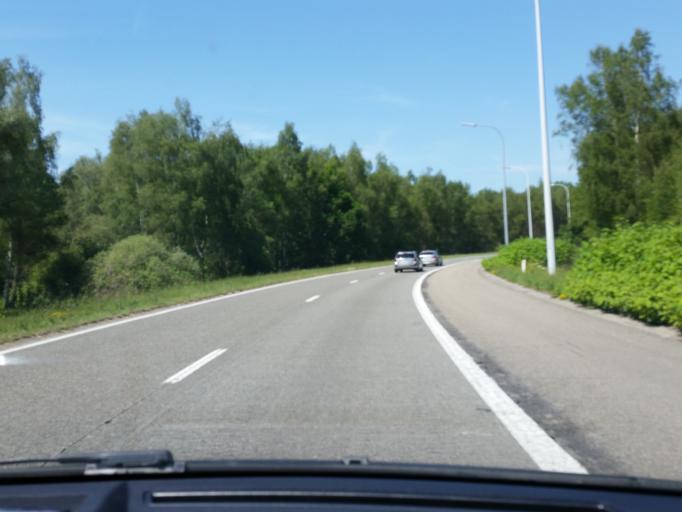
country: BE
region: Flanders
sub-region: Provincie Antwerpen
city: Mechelen
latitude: 51.0392
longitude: 4.4577
